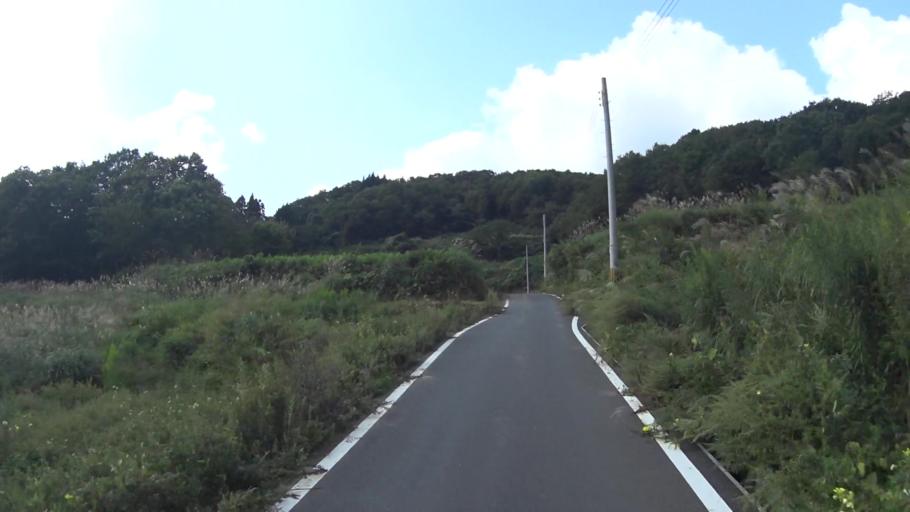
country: JP
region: Kyoto
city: Miyazu
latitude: 35.6414
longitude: 135.1816
